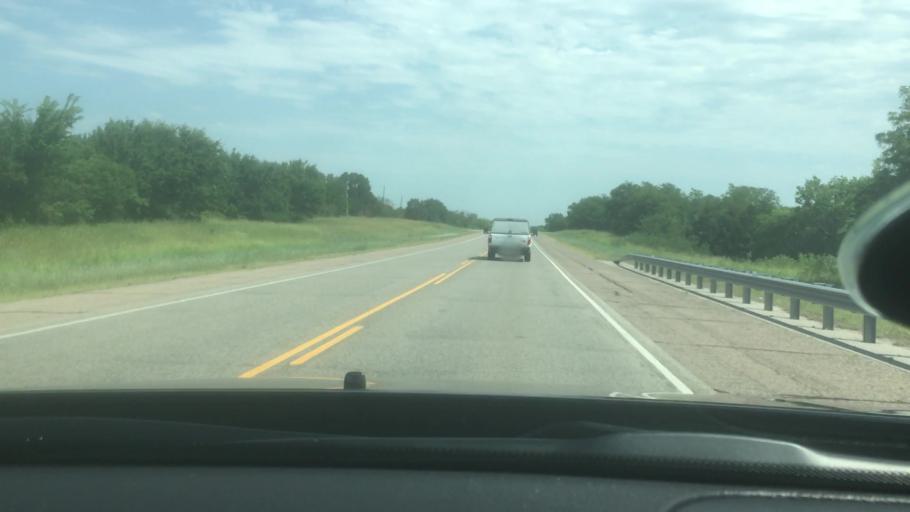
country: US
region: Oklahoma
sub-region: Seminole County
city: Maud
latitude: 35.0450
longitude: -96.9314
